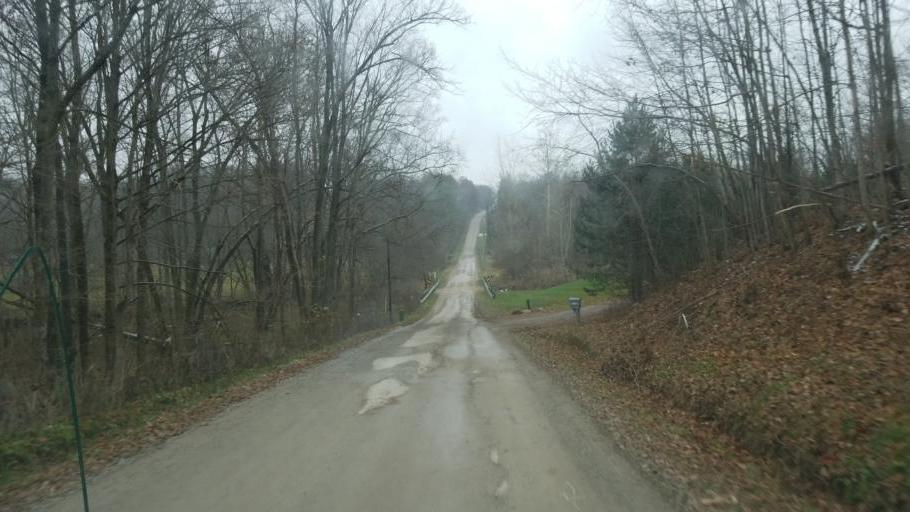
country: US
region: Ohio
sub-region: Huron County
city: New London
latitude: 40.9754
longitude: -82.3832
